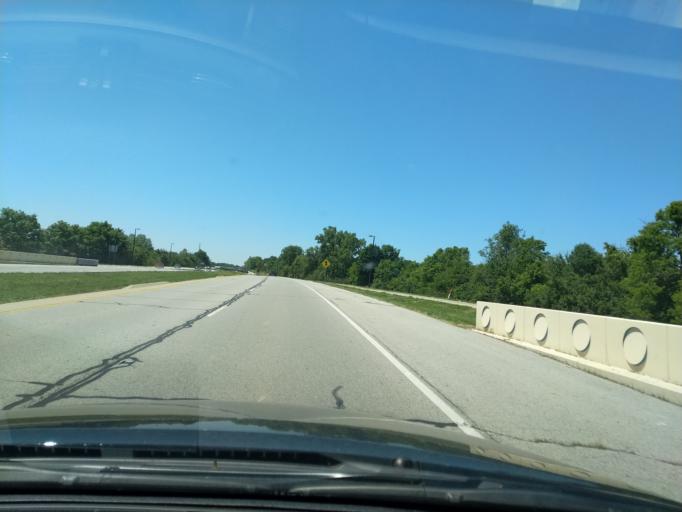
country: US
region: Indiana
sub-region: Hamilton County
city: Carmel
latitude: 39.9870
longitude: -86.1153
